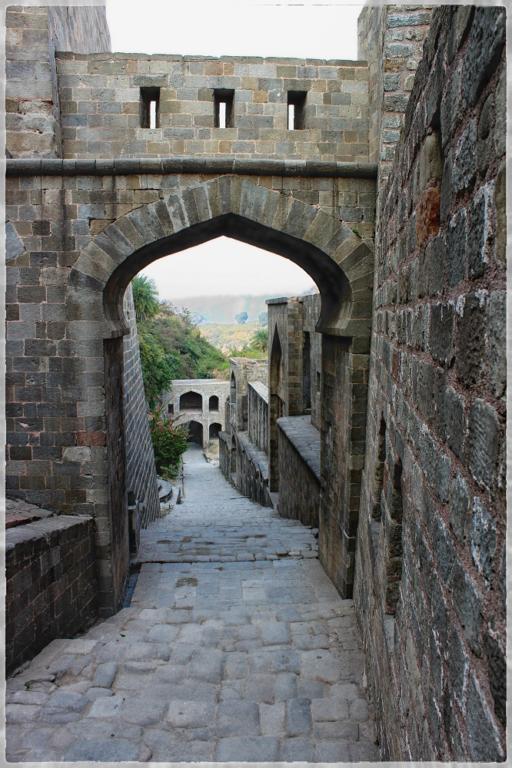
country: IN
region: Himachal Pradesh
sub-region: Kangra
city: Kangra
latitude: 32.0865
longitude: 76.2545
